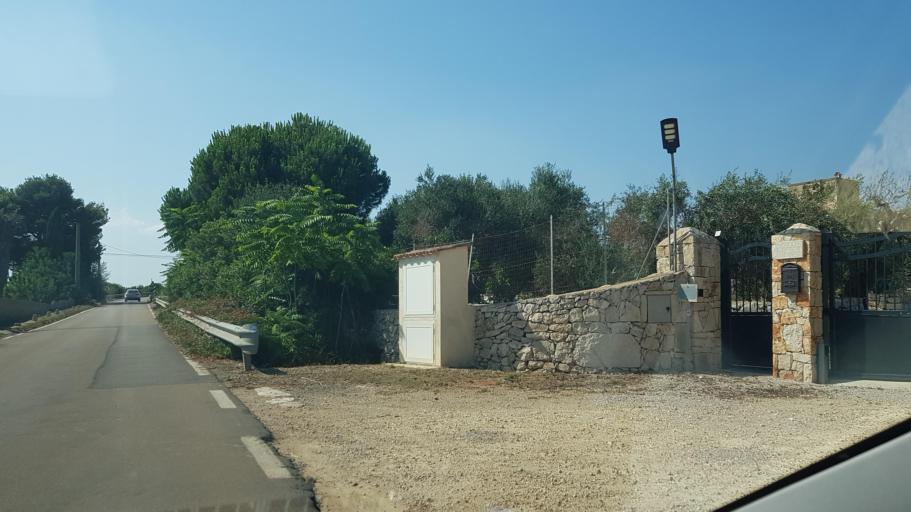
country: IT
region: Apulia
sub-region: Provincia di Lecce
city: Gemini
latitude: 39.8460
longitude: 18.2087
